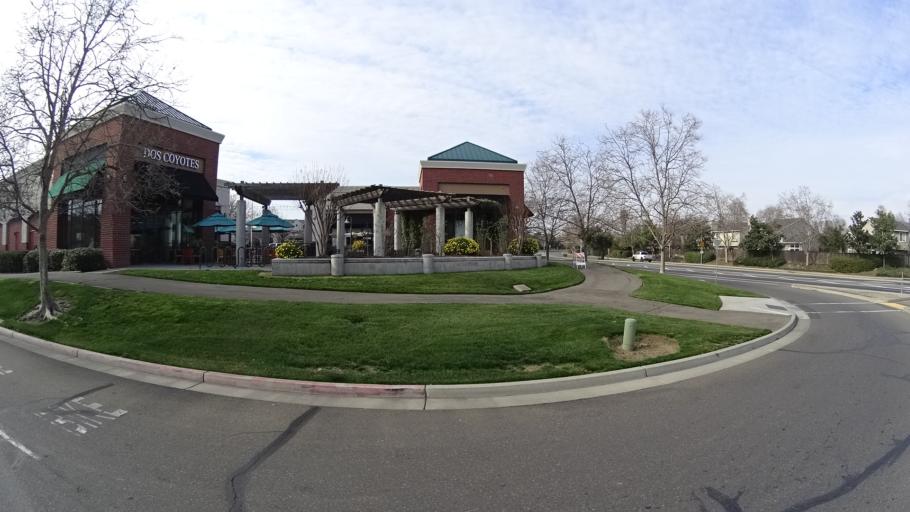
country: US
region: California
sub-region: Yolo County
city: Davis
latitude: 38.5411
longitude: -121.7233
